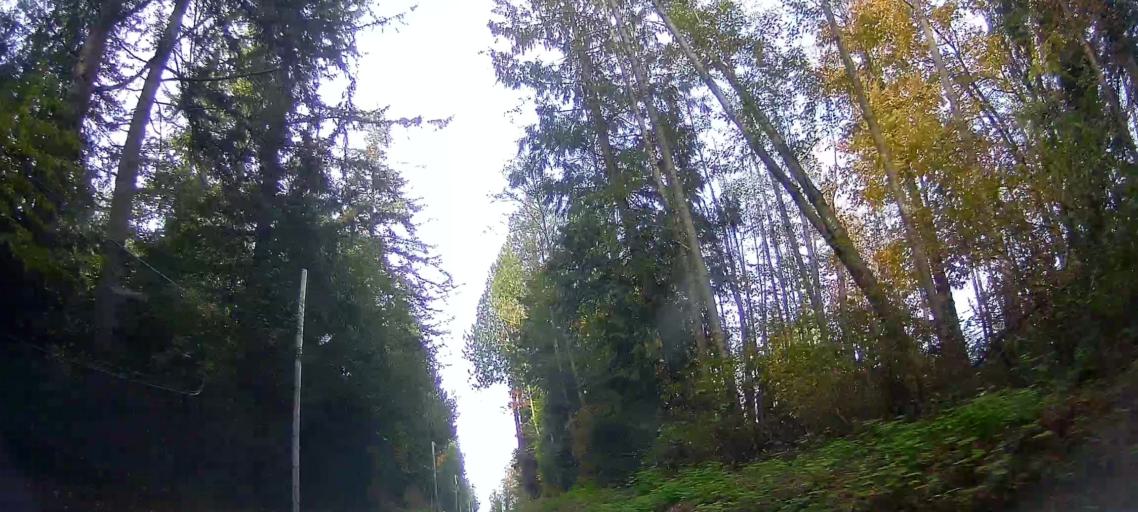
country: US
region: Washington
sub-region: Snohomish County
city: Stanwood
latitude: 48.2632
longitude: -122.3414
